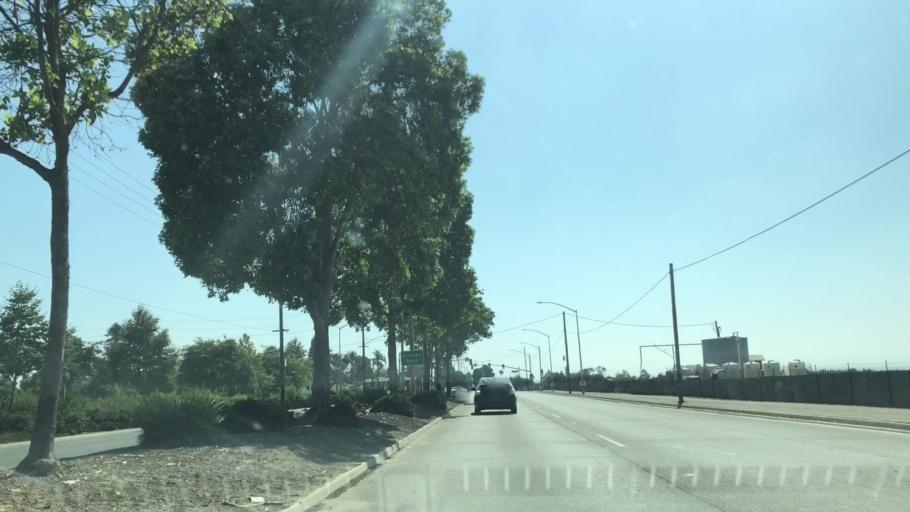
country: US
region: California
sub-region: Ventura County
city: El Rio
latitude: 34.2685
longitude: -119.1907
